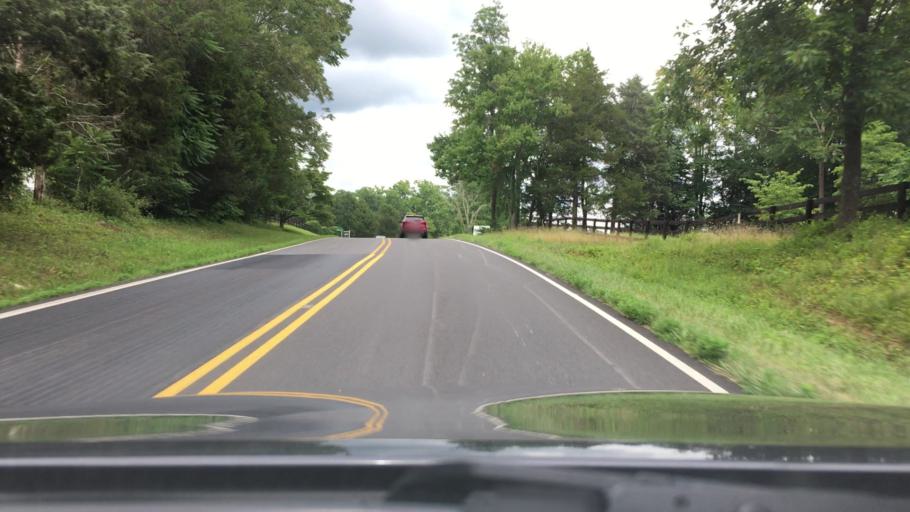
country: US
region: Virginia
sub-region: Orange County
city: Gordonsville
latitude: 38.1200
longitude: -78.2237
